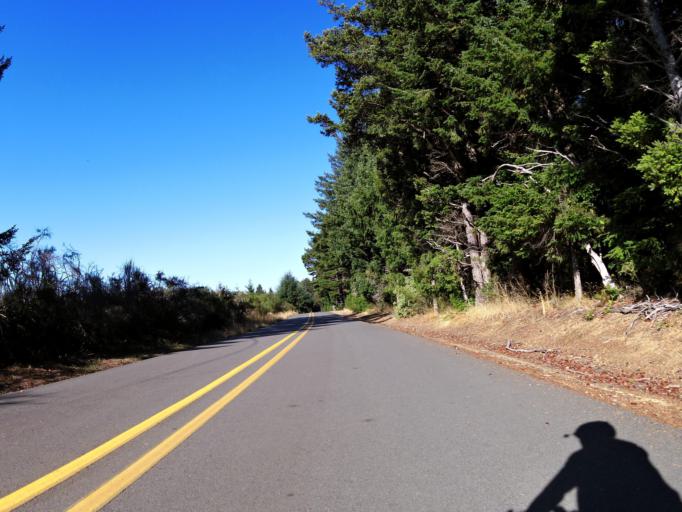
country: US
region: Oregon
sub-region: Coos County
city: Bandon
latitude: 43.0396
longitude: -124.4082
